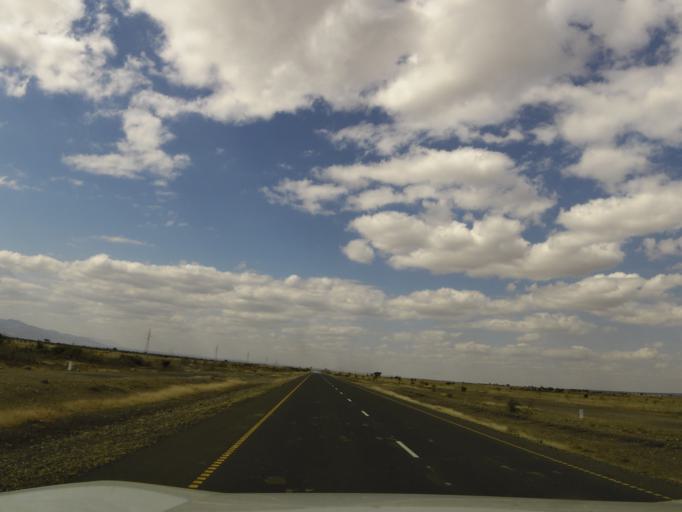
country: TZ
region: Arusha
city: Mto wa Mbu
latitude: -3.6206
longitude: 36.0283
